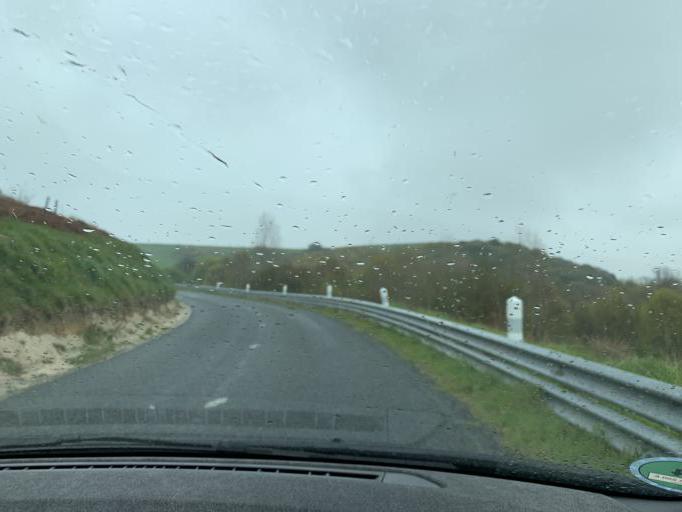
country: FR
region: Haute-Normandie
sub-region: Departement de la Seine-Maritime
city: Etretat
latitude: 49.7120
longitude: 0.2284
